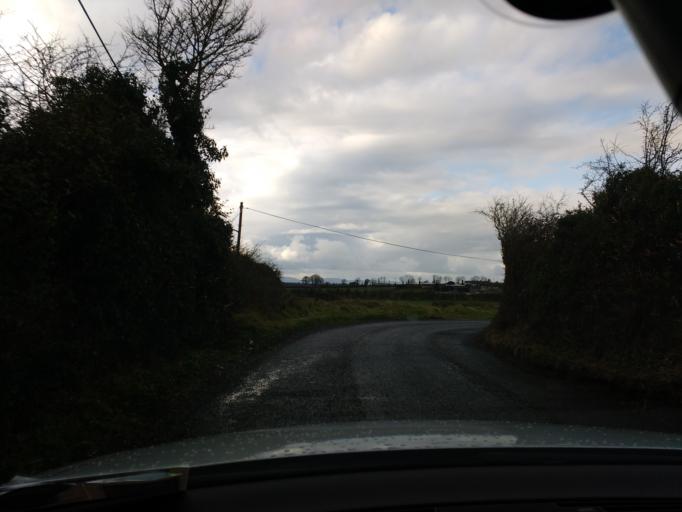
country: IE
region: Leinster
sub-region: Laois
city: Rathdowney
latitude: 52.6779
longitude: -7.6061
